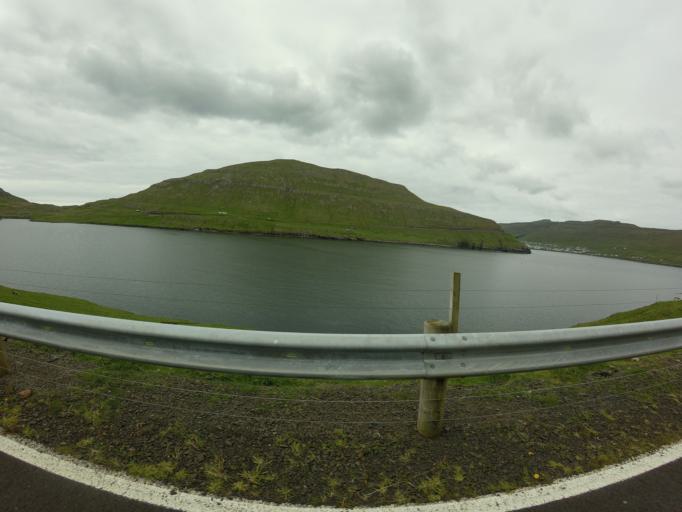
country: FO
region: Suduroy
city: Vagur
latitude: 61.4514
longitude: -6.7643
